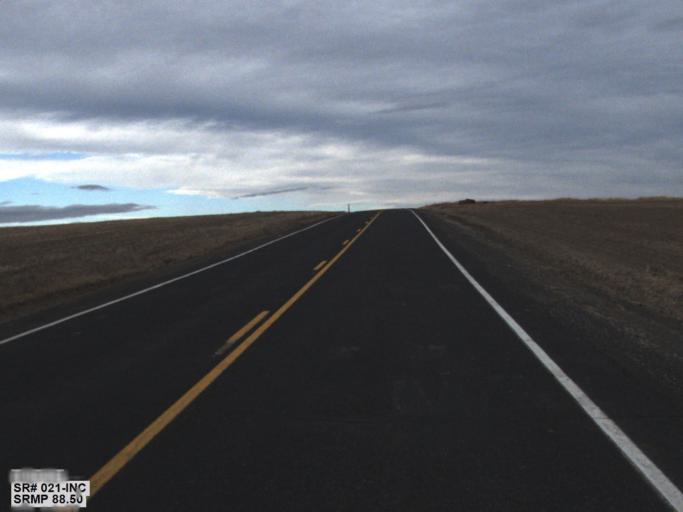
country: US
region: Washington
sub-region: Okanogan County
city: Coulee Dam
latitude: 47.7196
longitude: -118.7220
